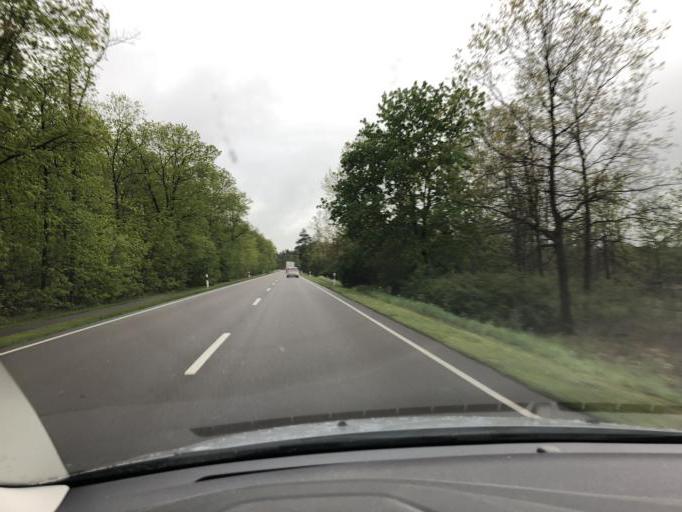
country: DE
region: Saxony-Anhalt
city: Dessau
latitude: 51.7693
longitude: 12.2301
